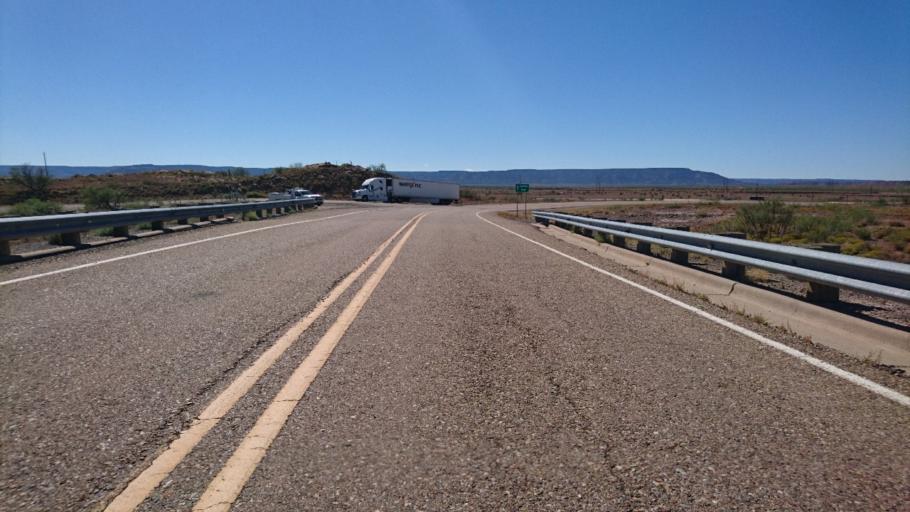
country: US
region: New Mexico
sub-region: Quay County
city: Tucumcari
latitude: 35.0929
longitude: -104.0706
